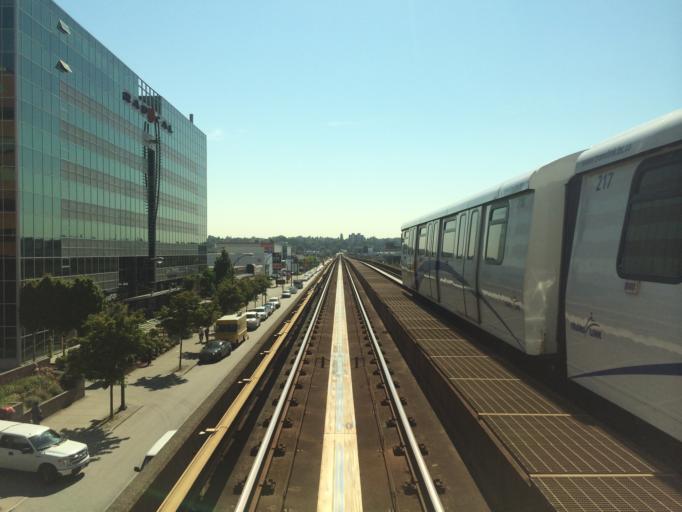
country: CA
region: British Columbia
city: Vancouver
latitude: 49.2722
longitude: -123.0958
